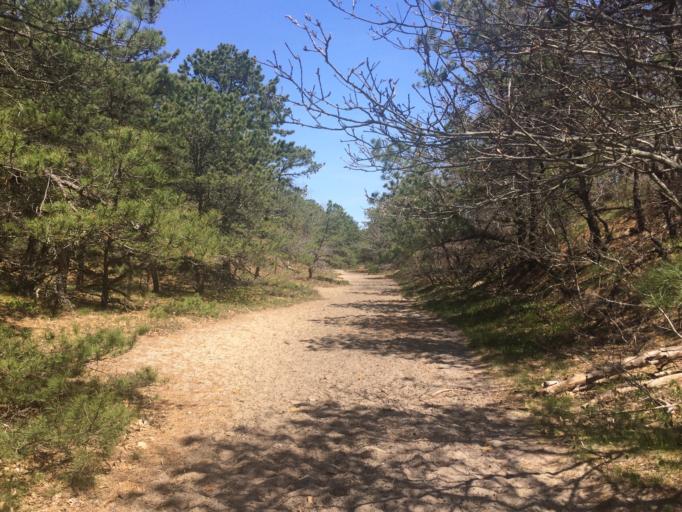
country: US
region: Massachusetts
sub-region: Barnstable County
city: Provincetown
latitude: 42.0630
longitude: -70.1740
